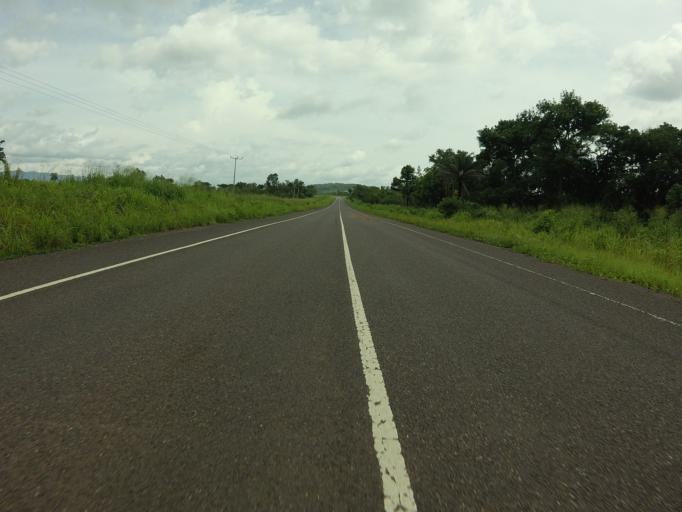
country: TG
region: Plateaux
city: Badou
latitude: 7.9633
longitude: 0.5566
